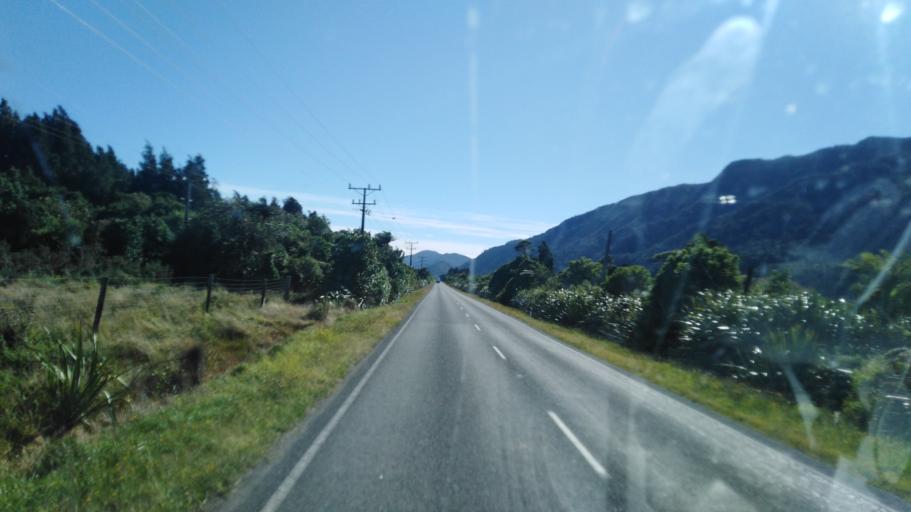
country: NZ
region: West Coast
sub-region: Buller District
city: Westport
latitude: -41.6623
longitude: 171.8154
